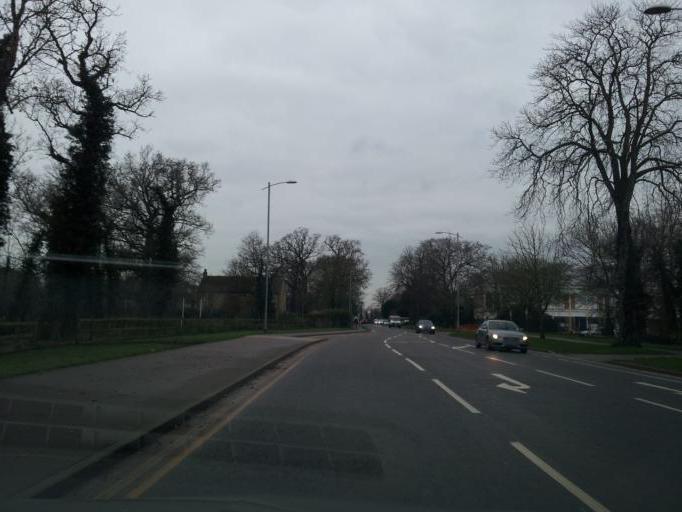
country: GB
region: England
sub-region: Cambridgeshire
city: Cambridge
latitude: 52.1802
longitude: 0.1219
